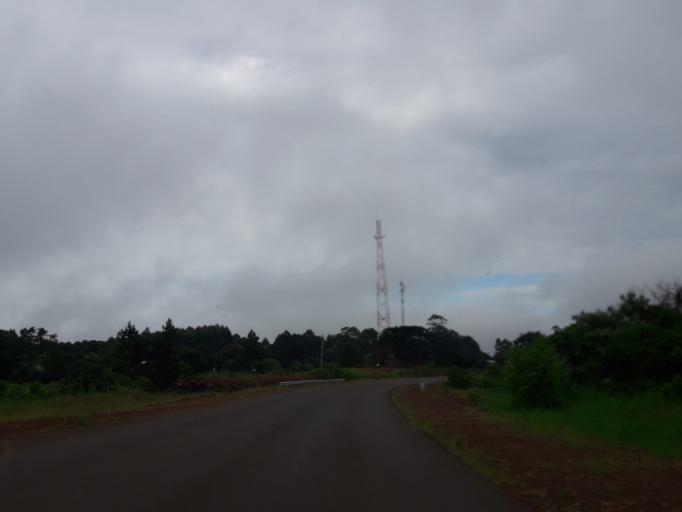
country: AR
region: Misiones
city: Bernardo de Irigoyen
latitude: -26.4242
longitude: -53.8400
